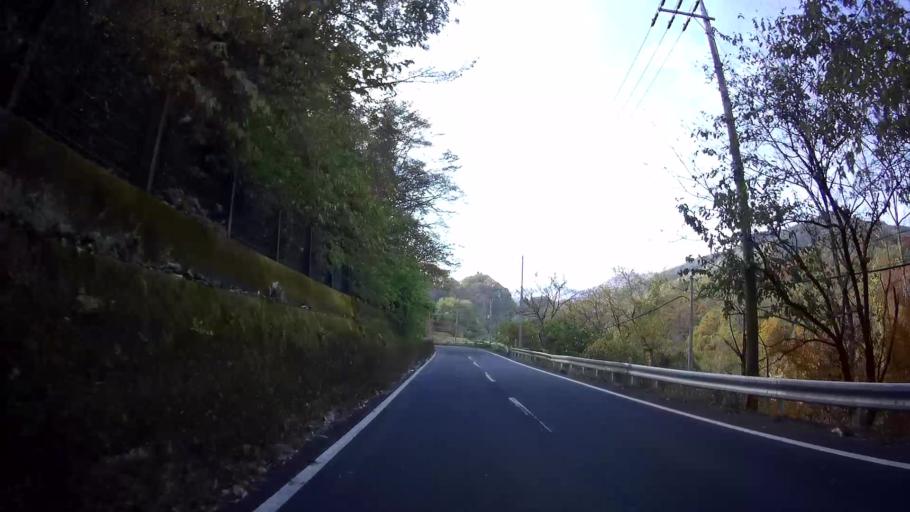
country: JP
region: Gunma
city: Nakanojomachi
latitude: 36.5066
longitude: 138.7379
